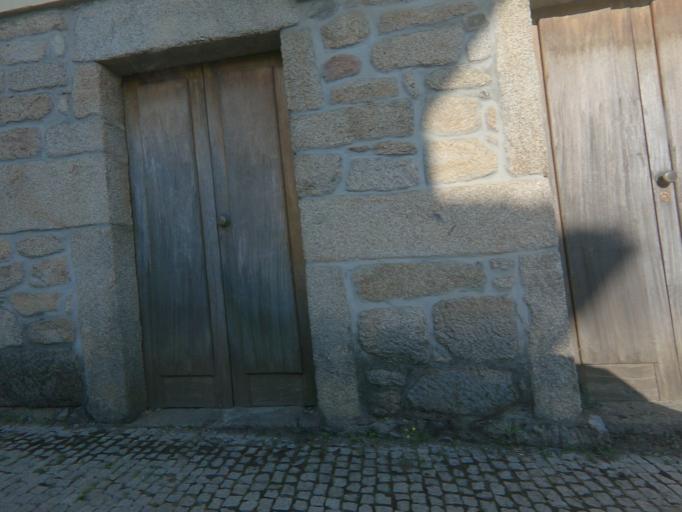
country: PT
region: Vila Real
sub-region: Sabrosa
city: Vilela
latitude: 41.2657
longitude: -7.6199
